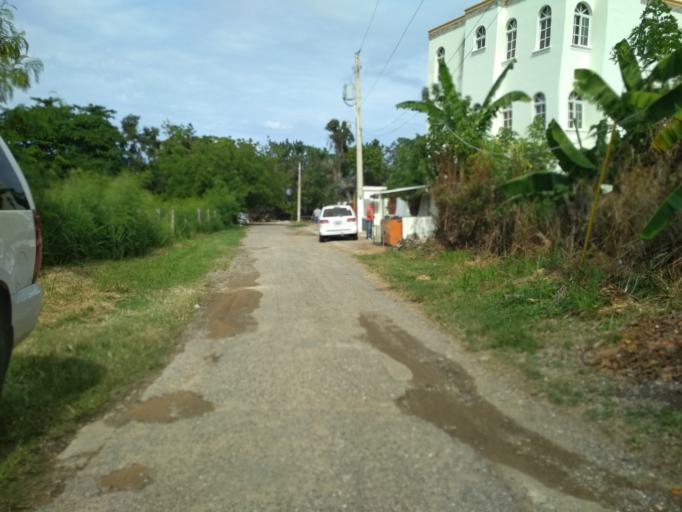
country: DO
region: Puerto Plata
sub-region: Puerto Plata
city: Puerto Plata
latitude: 19.8133
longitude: -70.7125
